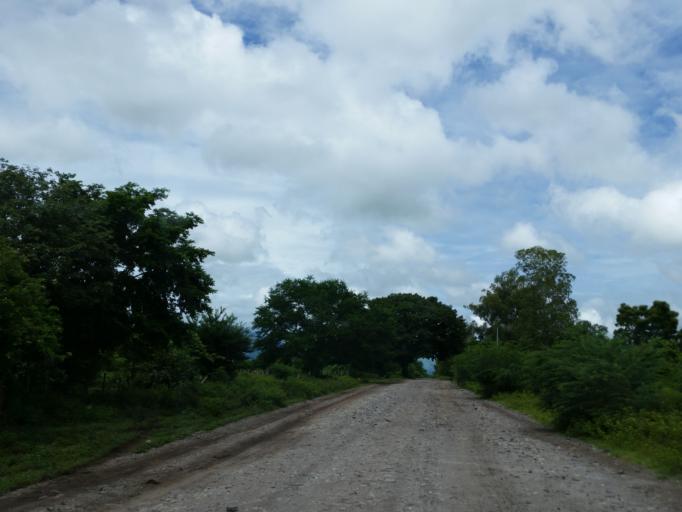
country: NI
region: Leon
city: Telica
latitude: 12.6661
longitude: -86.7899
